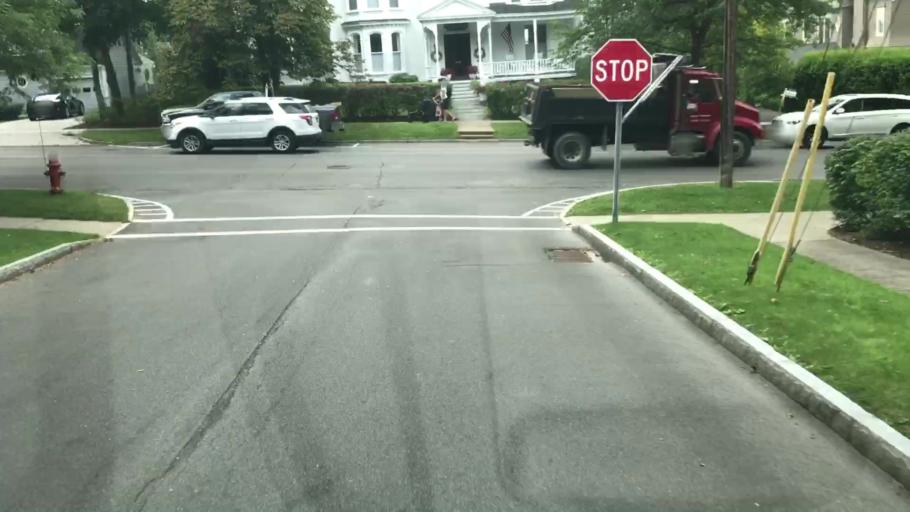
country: US
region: New York
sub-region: Onondaga County
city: Skaneateles
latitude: 42.9455
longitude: -76.4239
